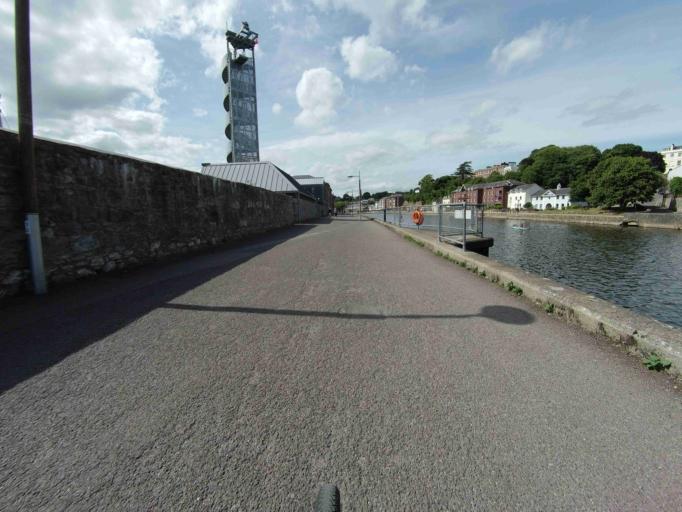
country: GB
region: England
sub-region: Devon
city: Exeter
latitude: 50.7161
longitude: -3.5281
